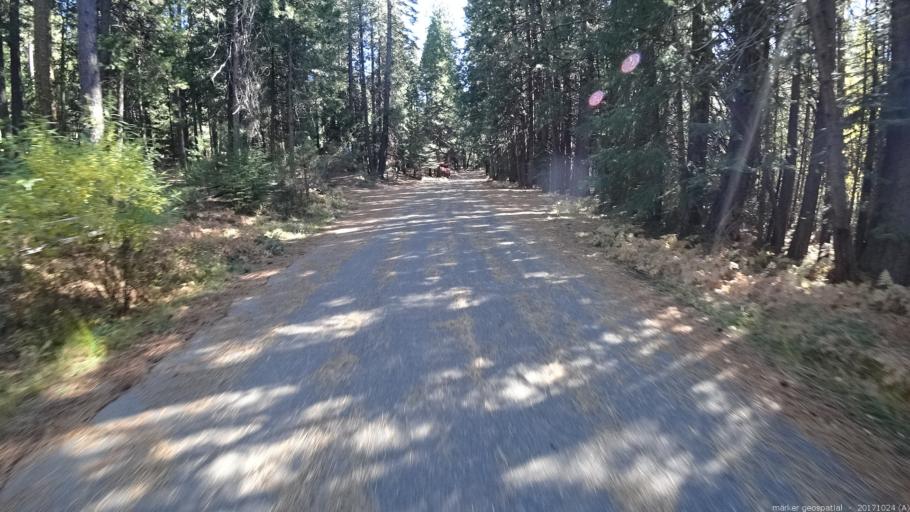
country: US
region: California
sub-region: Shasta County
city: Shingletown
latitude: 40.5180
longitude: -121.6782
